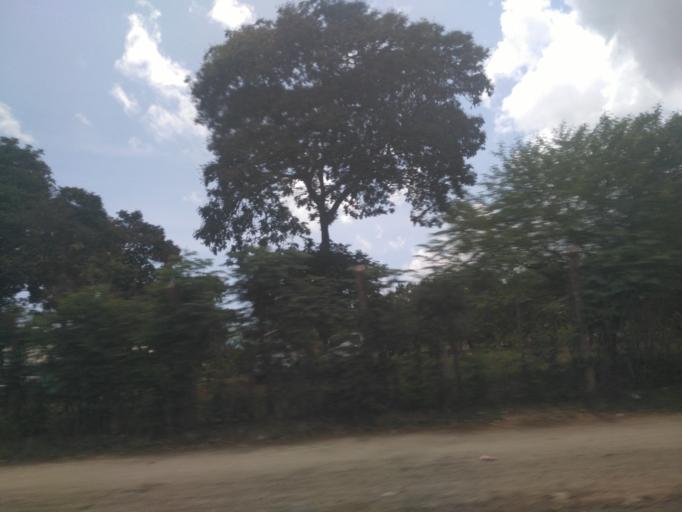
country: TZ
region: Dar es Salaam
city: Dar es Salaam
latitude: -6.8498
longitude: 39.2714
